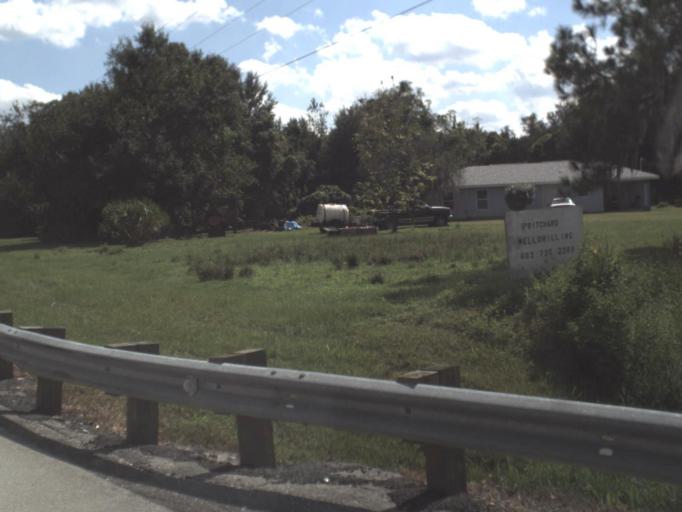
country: US
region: Florida
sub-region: Hardee County
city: Zolfo Springs
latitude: 27.4926
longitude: -81.7723
